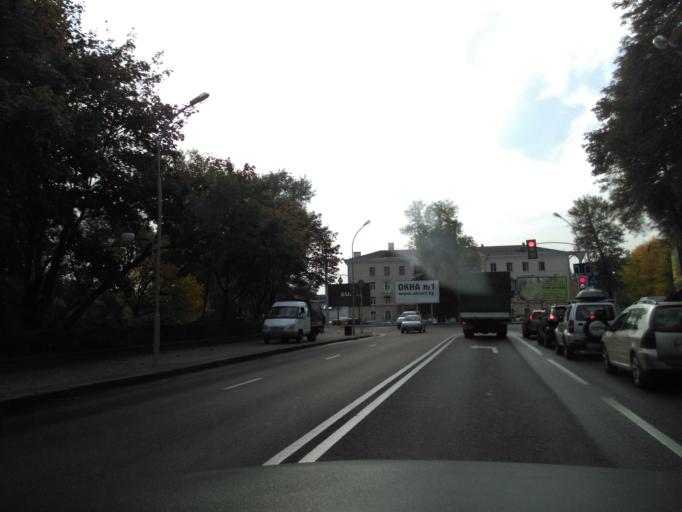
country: BY
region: Minsk
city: Minsk
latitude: 53.8996
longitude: 27.5715
